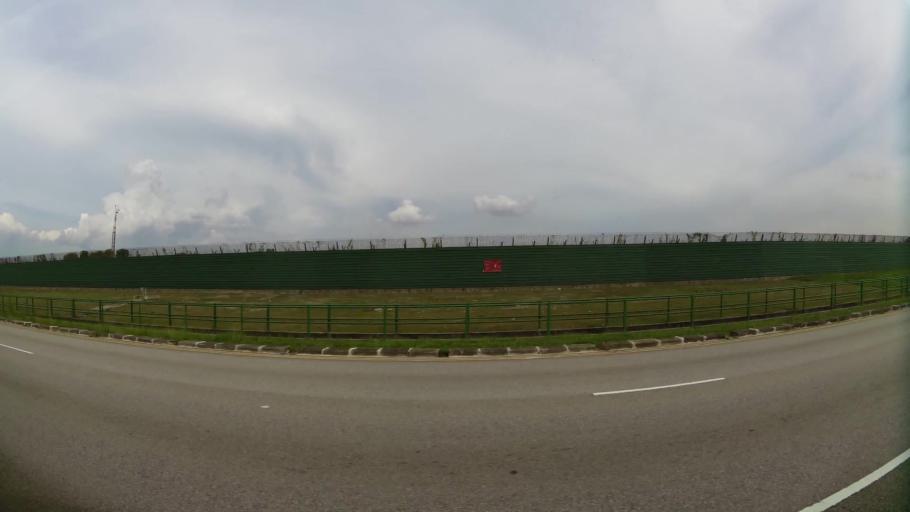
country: MY
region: Johor
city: Johor Bahru
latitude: 1.3874
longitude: 103.6980
